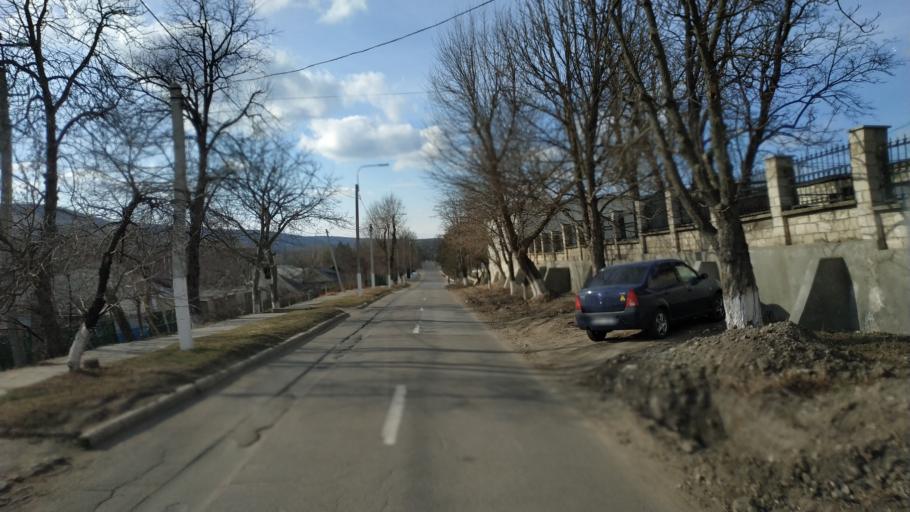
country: MD
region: Hincesti
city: Hincesti
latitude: 46.8339
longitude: 28.5799
